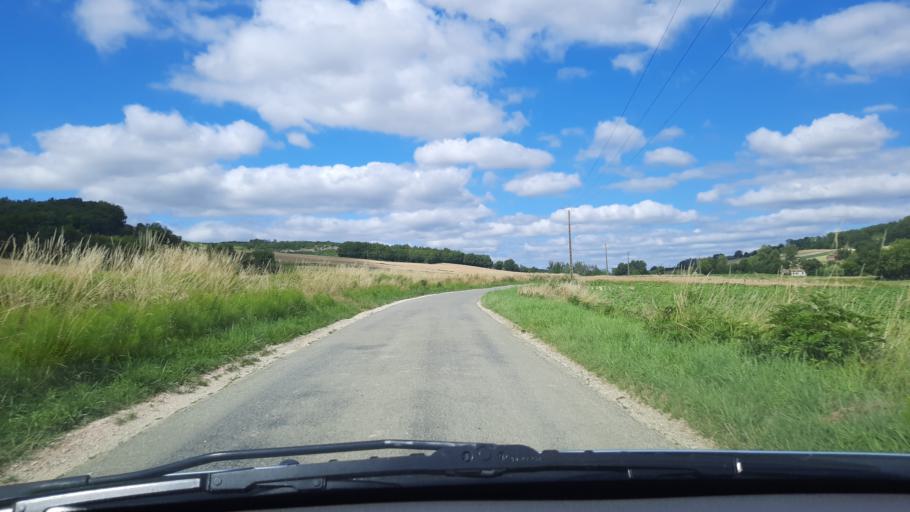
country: FR
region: Midi-Pyrenees
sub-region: Departement du Lot
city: Castelnau-Montratier
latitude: 44.2752
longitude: 1.3974
